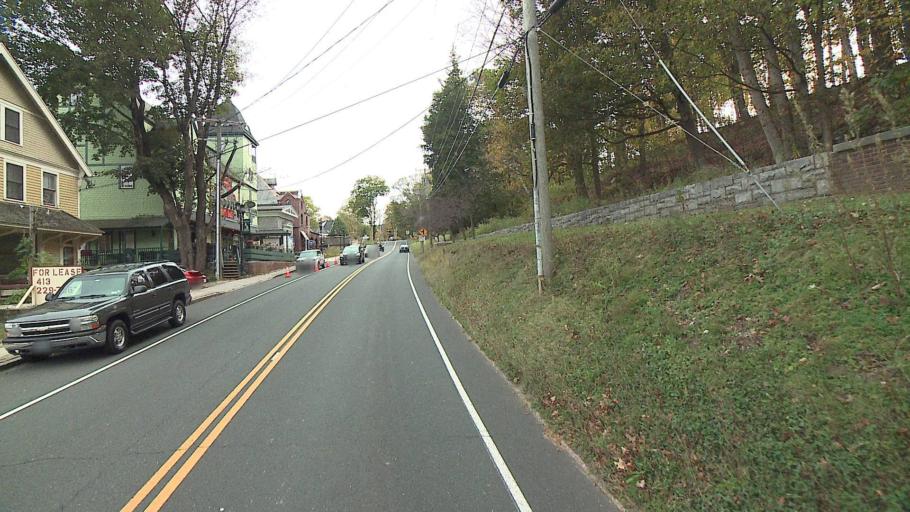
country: US
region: Connecticut
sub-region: Litchfield County
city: Winchester Center
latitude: 41.9911
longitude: -73.2004
